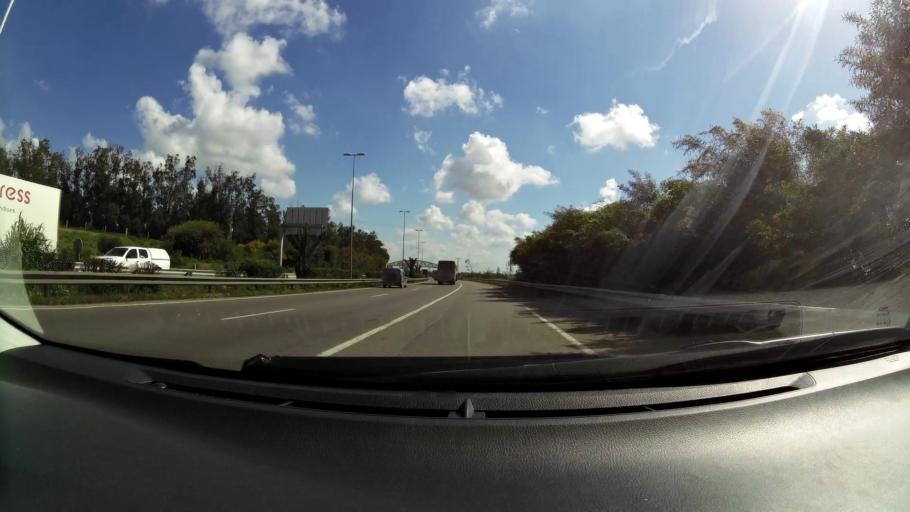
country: MA
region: Grand Casablanca
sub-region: Nouaceur
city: Bouskoura
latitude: 33.4809
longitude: -7.6333
